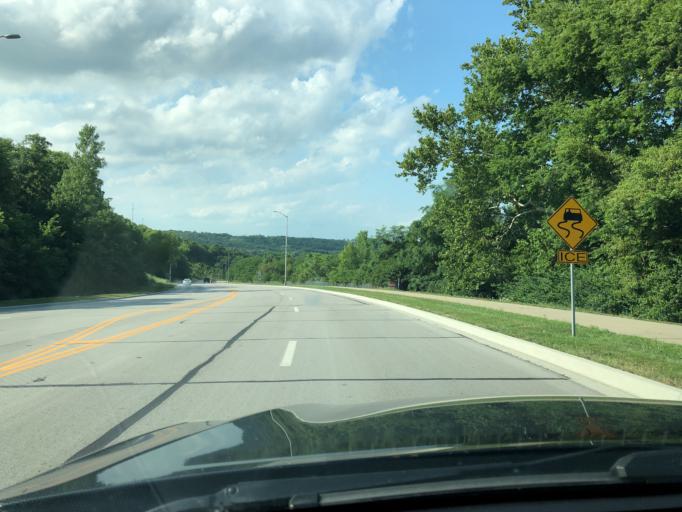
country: US
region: Kansas
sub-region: Leavenworth County
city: Leavenworth
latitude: 39.3013
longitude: -94.9525
